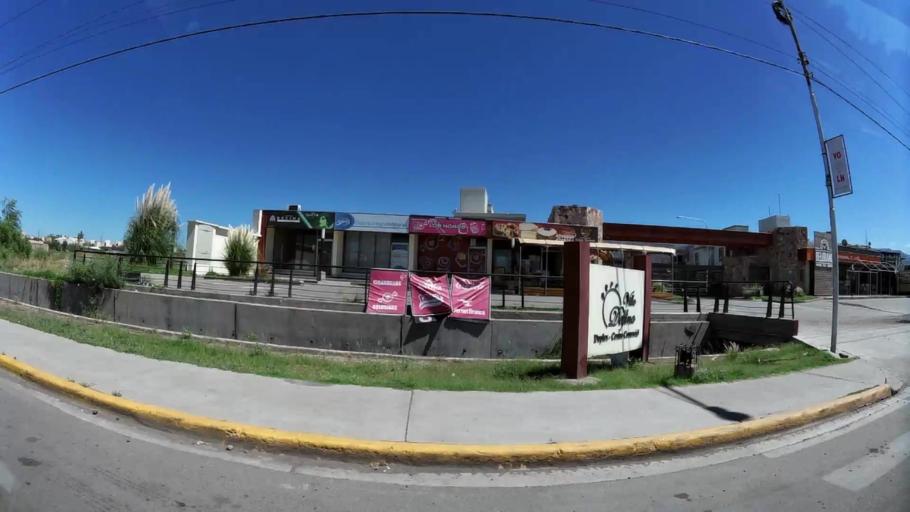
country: AR
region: Mendoza
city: Las Heras
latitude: -32.8472
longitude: -68.8607
